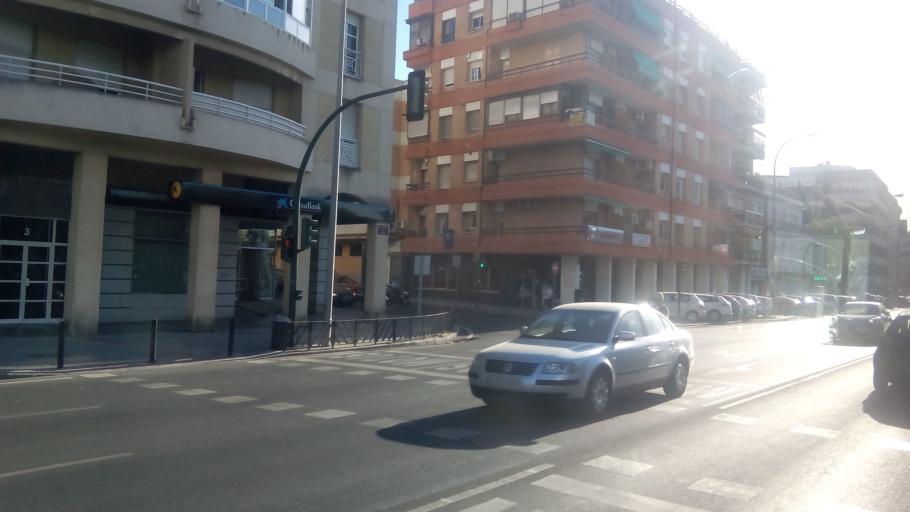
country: ES
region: Andalusia
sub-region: Province of Cordoba
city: Cordoba
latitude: 37.8921
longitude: -4.7760
